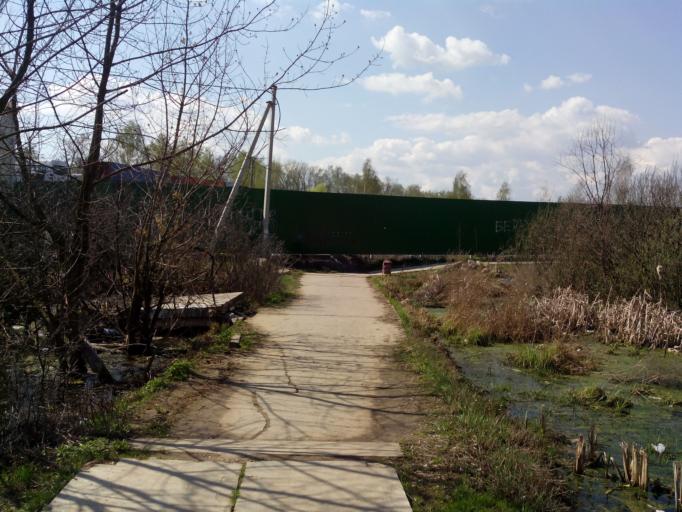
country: RU
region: Moskovskaya
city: Odintsovo
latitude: 55.6674
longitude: 37.2501
